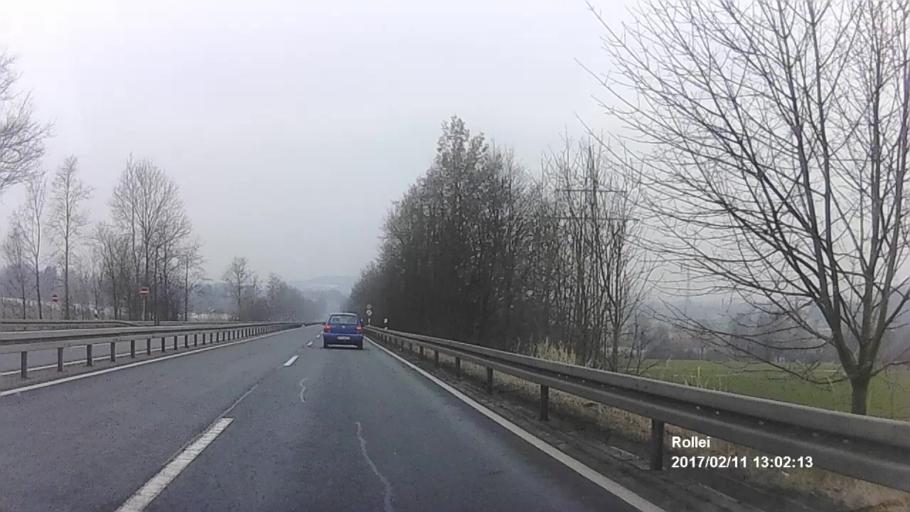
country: DE
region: Lower Saxony
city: Gittelde
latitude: 51.7976
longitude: 10.1957
